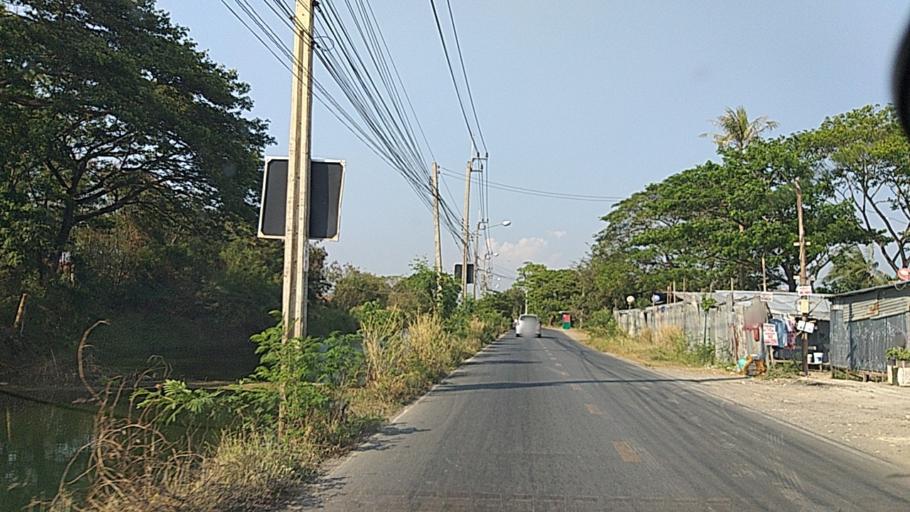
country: TH
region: Nonthaburi
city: Sai Noi
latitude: 13.9416
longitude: 100.3500
